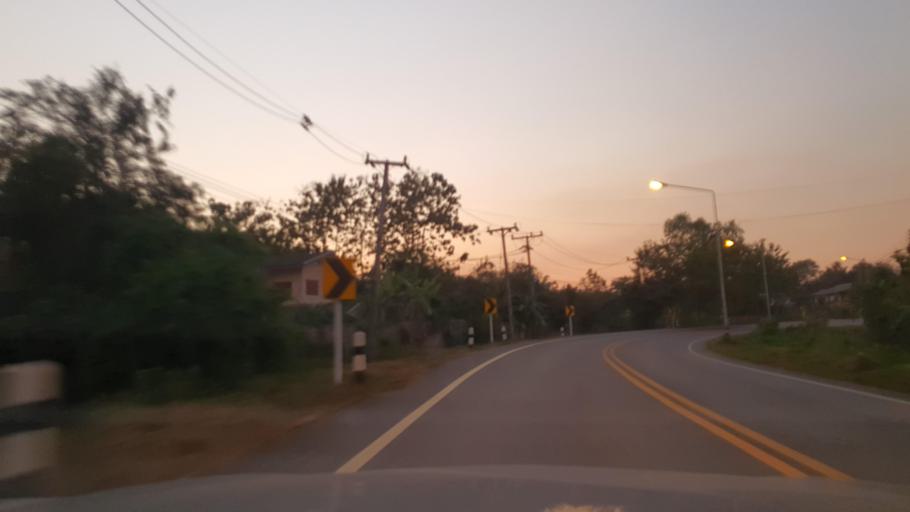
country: TH
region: Phayao
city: Dok Kham Tai
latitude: 19.1479
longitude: 100.0003
